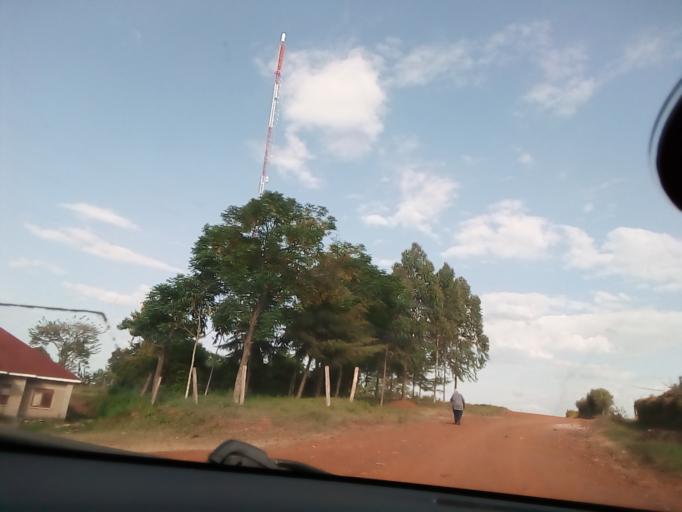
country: UG
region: Central Region
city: Masaka
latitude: -0.3619
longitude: 31.7507
